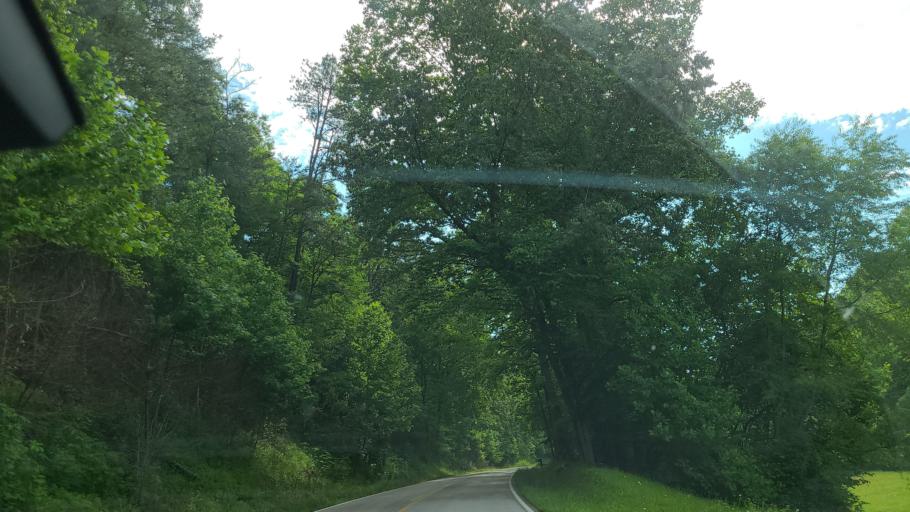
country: US
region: Kentucky
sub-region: Knox County
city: Barbourville
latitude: 36.6815
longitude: -83.9251
